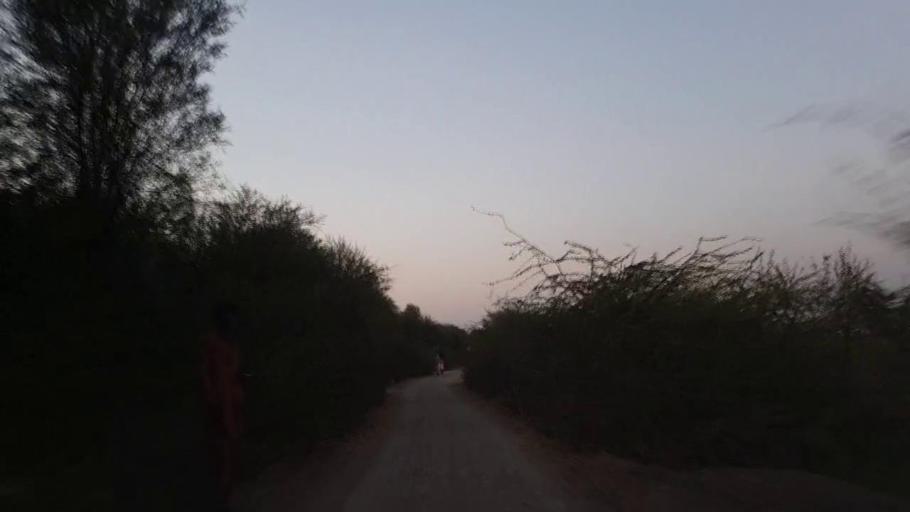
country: PK
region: Sindh
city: Naukot
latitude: 24.8904
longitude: 69.3844
